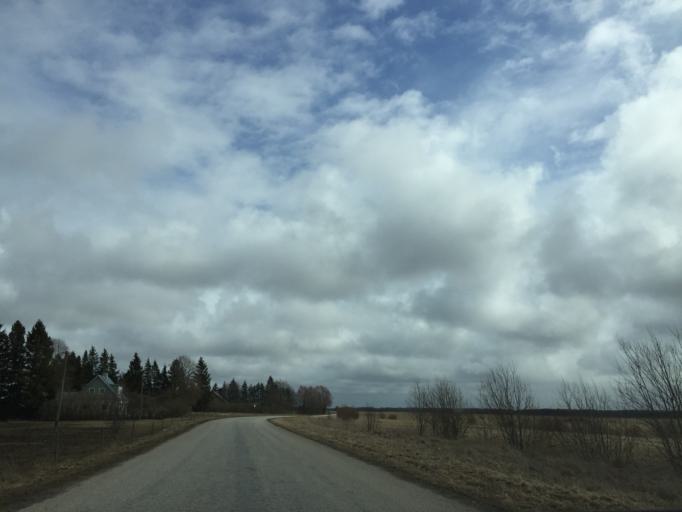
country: EE
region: Laeaene
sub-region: Lihula vald
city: Lihula
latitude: 58.7325
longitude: 23.8702
